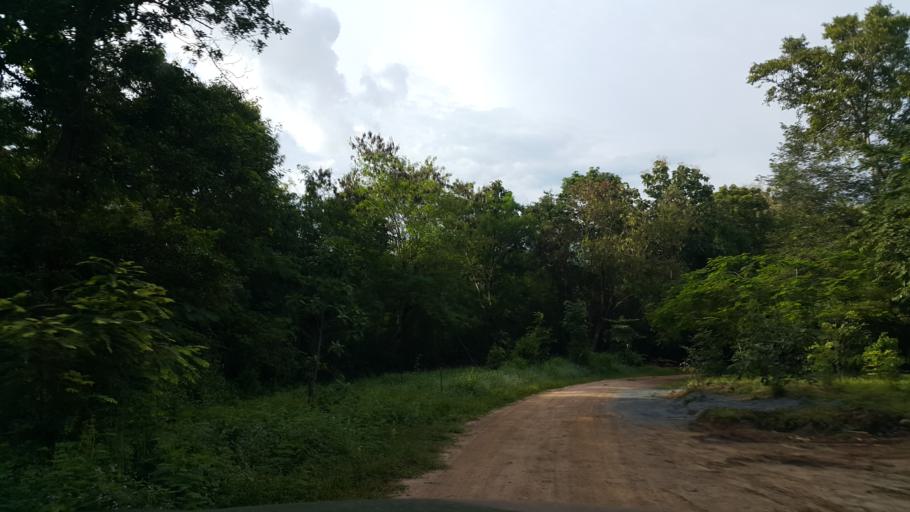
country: TH
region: Chiang Mai
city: Mae On
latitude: 18.8745
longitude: 99.2140
